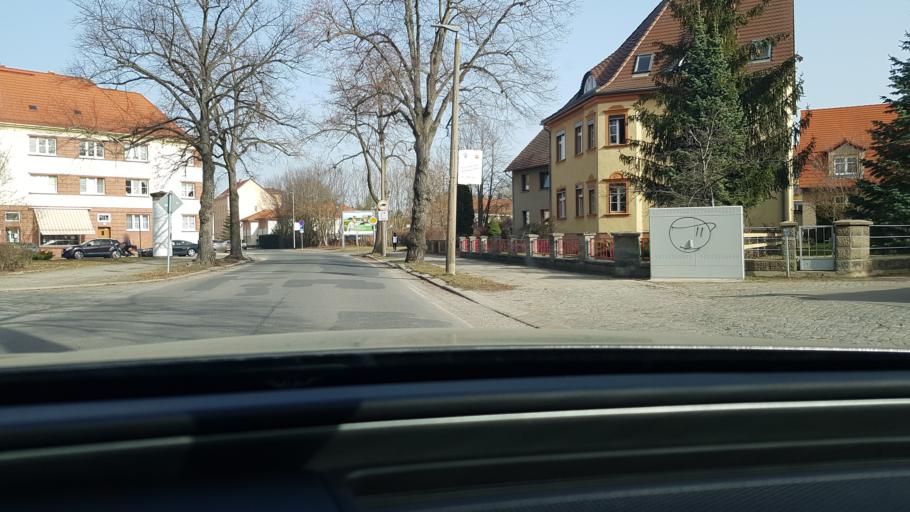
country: DE
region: Brandenburg
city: Guben
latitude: 51.9425
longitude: 14.7069
